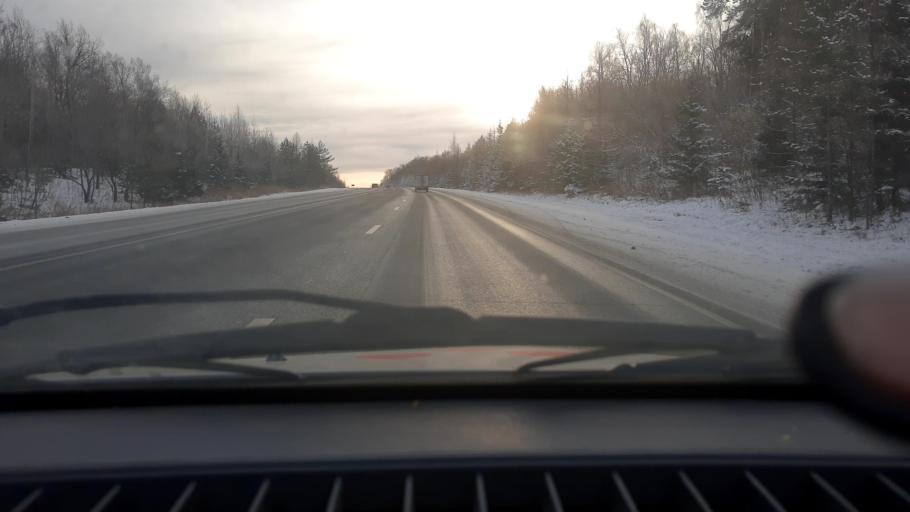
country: RU
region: Bashkortostan
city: Avdon
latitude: 54.8466
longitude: 55.7080
